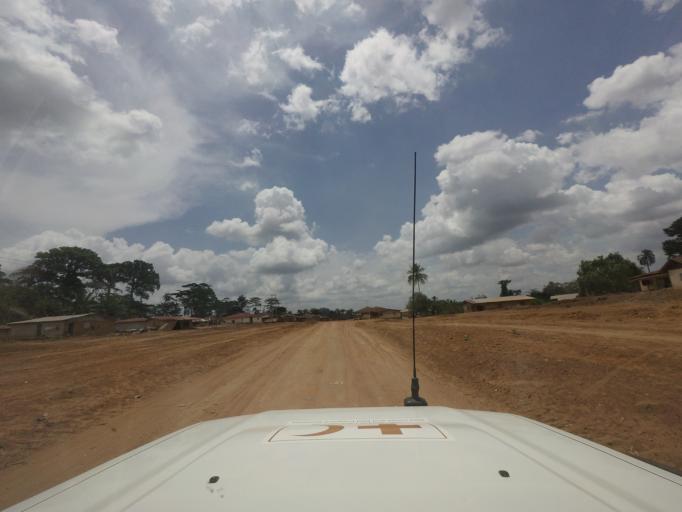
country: LR
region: Nimba
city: Sanniquellie
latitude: 7.2309
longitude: -8.8914
